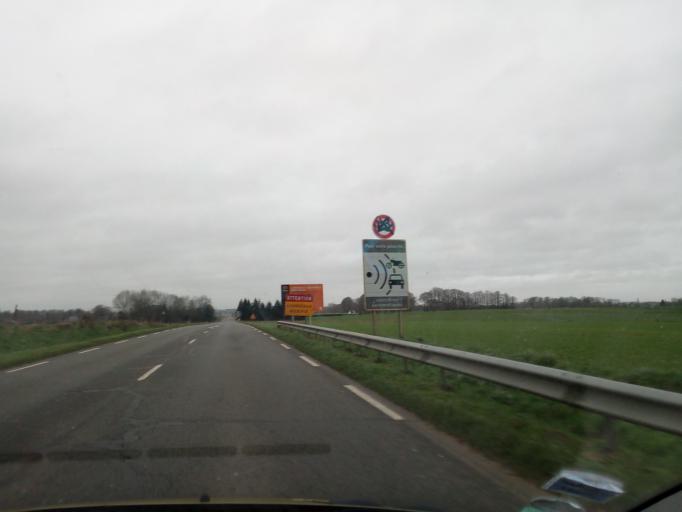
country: FR
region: Haute-Normandie
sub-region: Departement de la Seine-Maritime
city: Auzebosc
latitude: 49.5802
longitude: 0.7299
